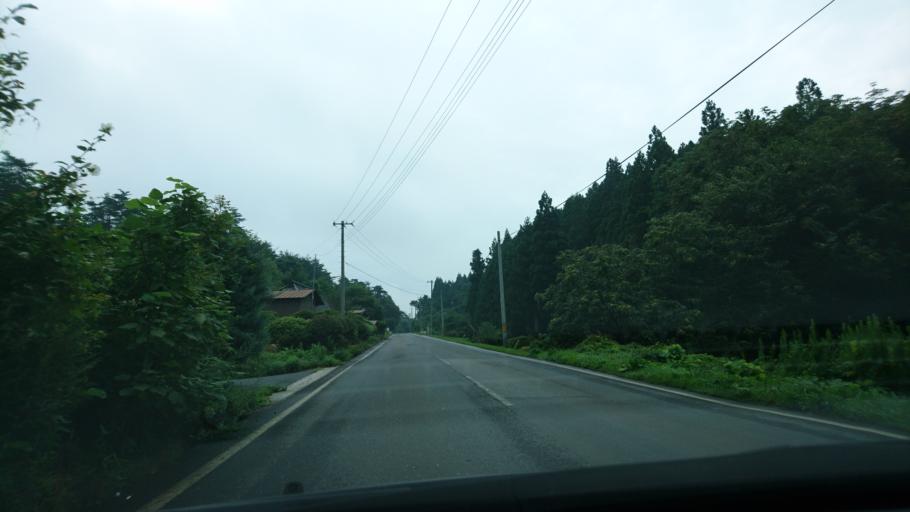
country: JP
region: Iwate
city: Ichinoseki
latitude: 38.9366
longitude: 141.1868
